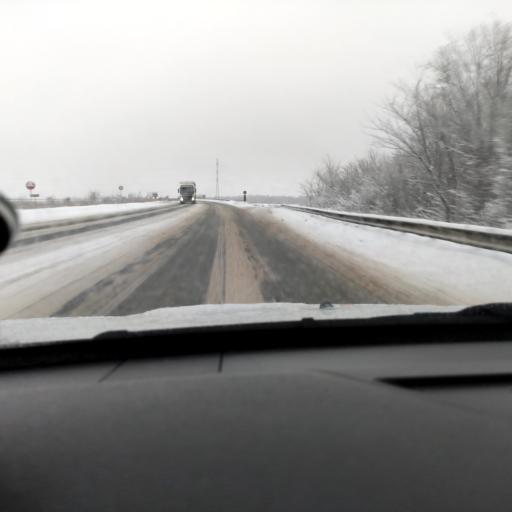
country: RU
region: Samara
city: Smyshlyayevka
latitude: 53.2566
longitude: 50.4756
